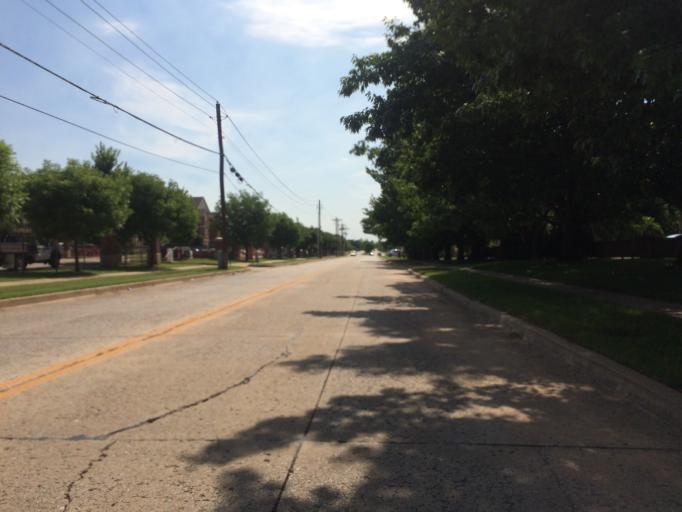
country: US
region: Oklahoma
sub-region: Cleveland County
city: Norman
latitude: 35.1894
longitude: -97.4532
